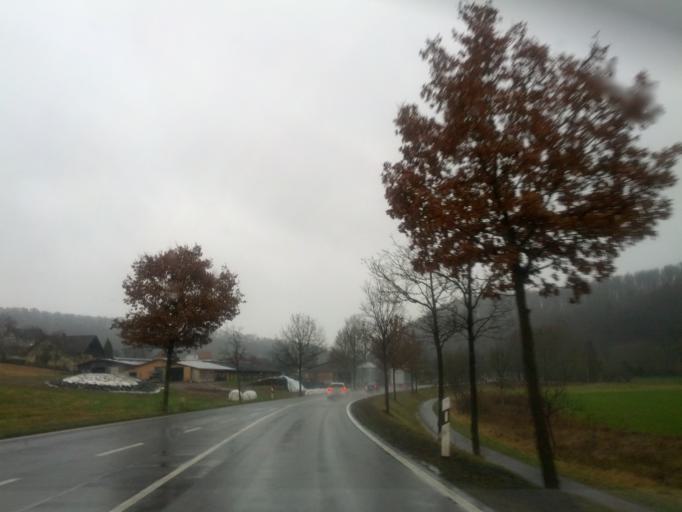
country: DE
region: Hesse
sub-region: Regierungsbezirk Kassel
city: Sontra
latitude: 51.0714
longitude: 9.9951
